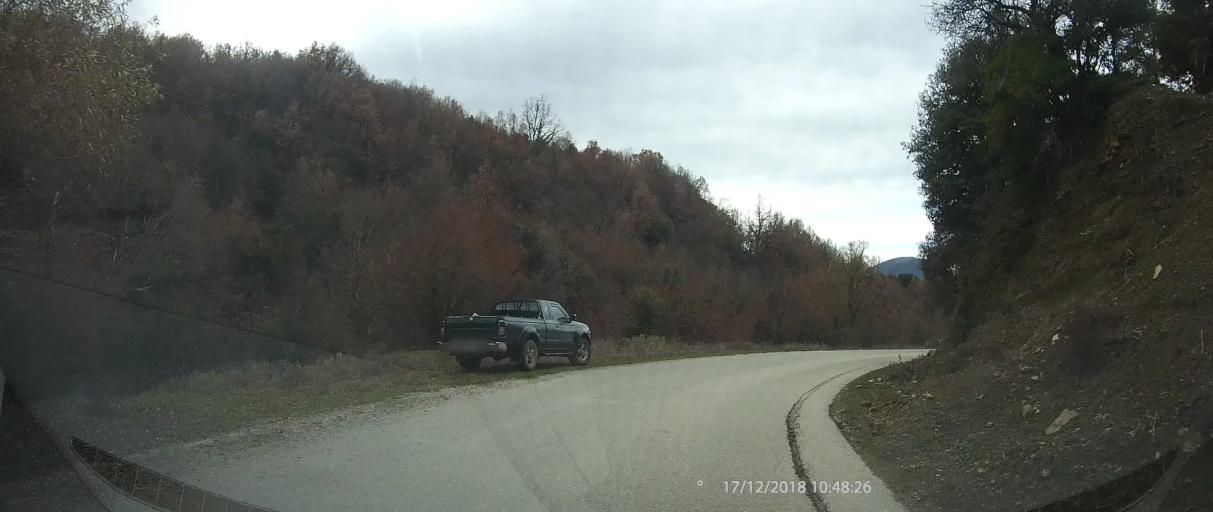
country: GR
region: Epirus
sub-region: Nomos Ioanninon
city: Konitsa
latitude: 39.9644
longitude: 20.7103
